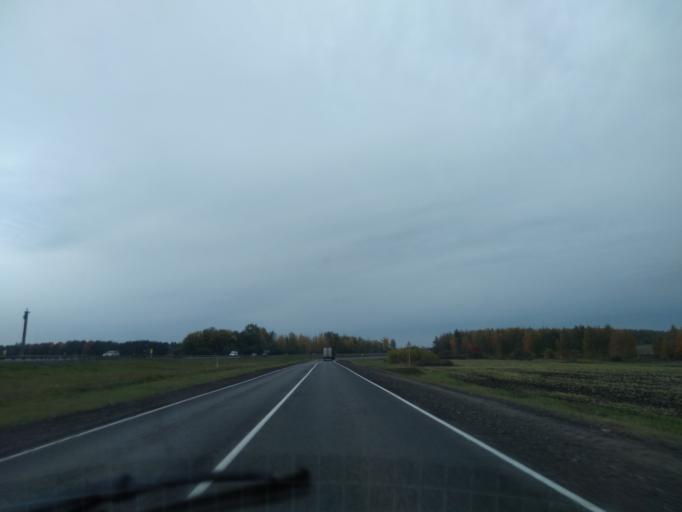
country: RU
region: Lipetsk
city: Zadonsk
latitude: 52.4435
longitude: 38.7908
